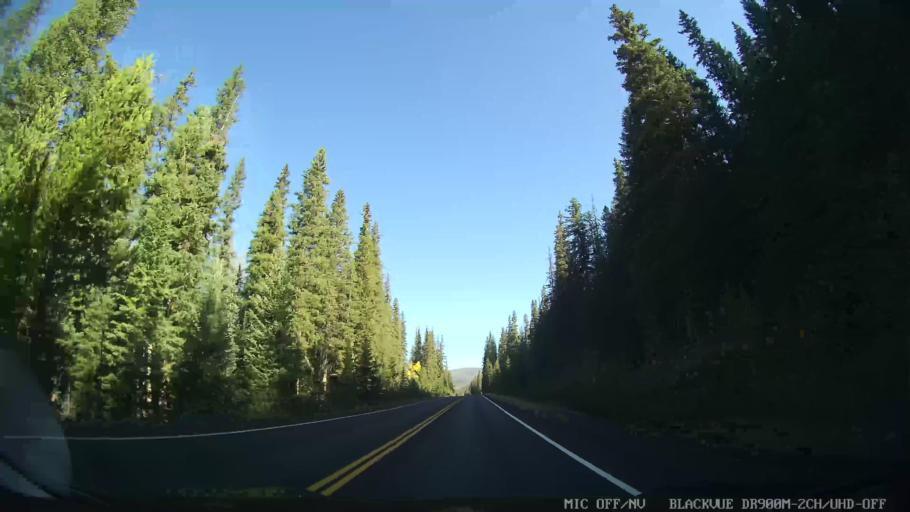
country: US
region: Colorado
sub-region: Grand County
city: Granby
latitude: 40.3003
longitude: -105.8430
